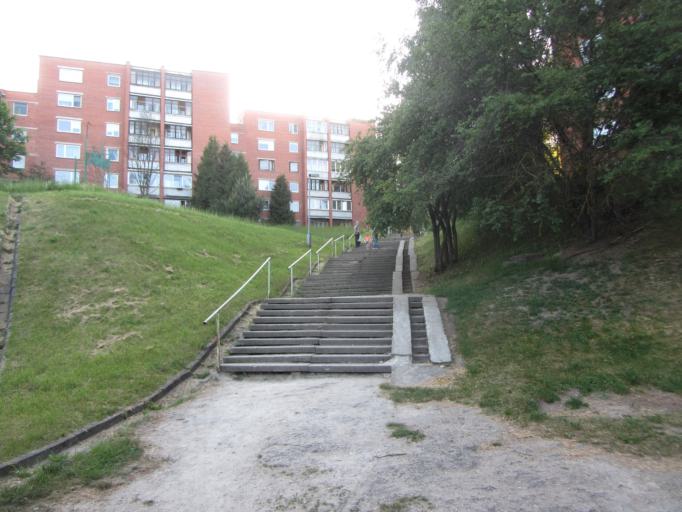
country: LT
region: Vilnius County
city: Seskine
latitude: 54.7266
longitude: 25.2759
